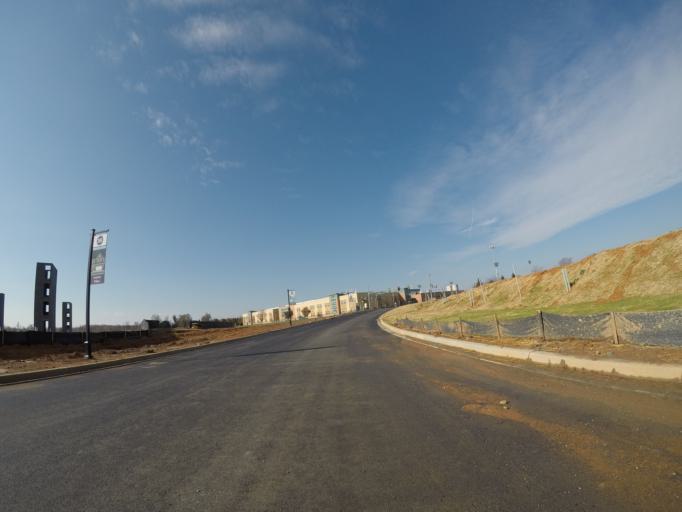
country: US
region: Maryland
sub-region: Frederick County
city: Ballenger Creek
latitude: 39.3779
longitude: -77.4430
